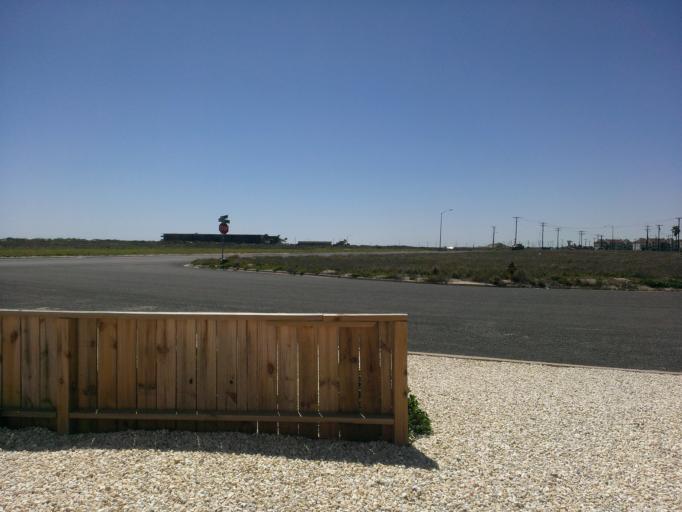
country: US
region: Texas
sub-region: Nueces County
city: Corpus Christi
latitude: 27.6039
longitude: -97.2109
